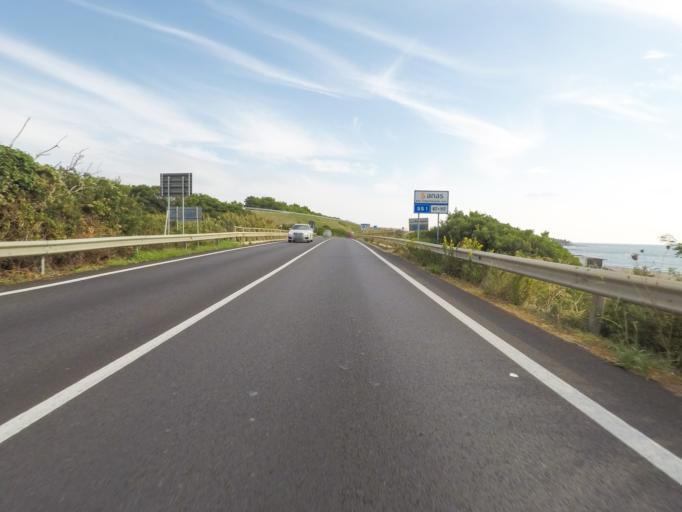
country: IT
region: Latium
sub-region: Citta metropolitana di Roma Capitale
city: Civitavecchia
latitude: 42.0577
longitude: 11.8188
